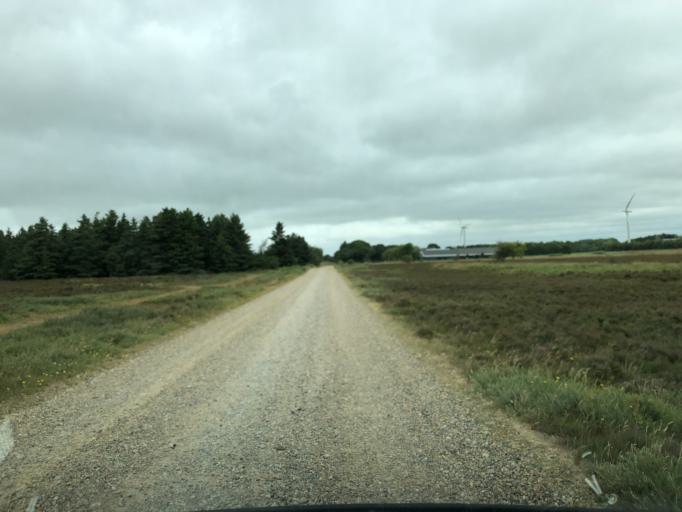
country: DK
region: Central Jutland
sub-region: Holstebro Kommune
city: Holstebro
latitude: 56.2337
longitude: 8.6208
